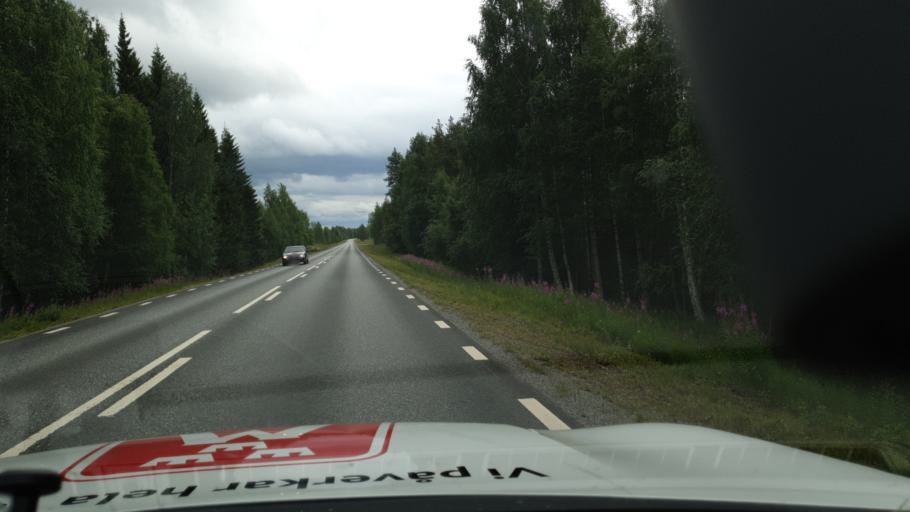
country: SE
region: Vaesterbotten
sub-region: Lycksele Kommun
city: Soderfors
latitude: 64.9231
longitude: 17.8213
